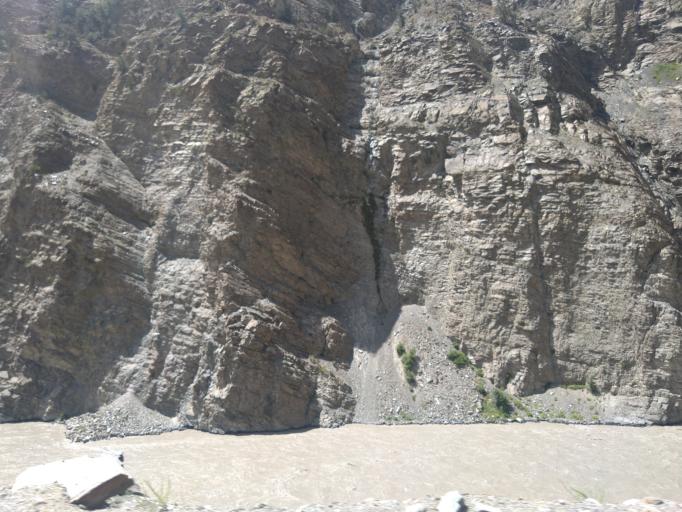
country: CN
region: Tibet Autonomous Region
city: Diyag
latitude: 31.6858
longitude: 78.4987
